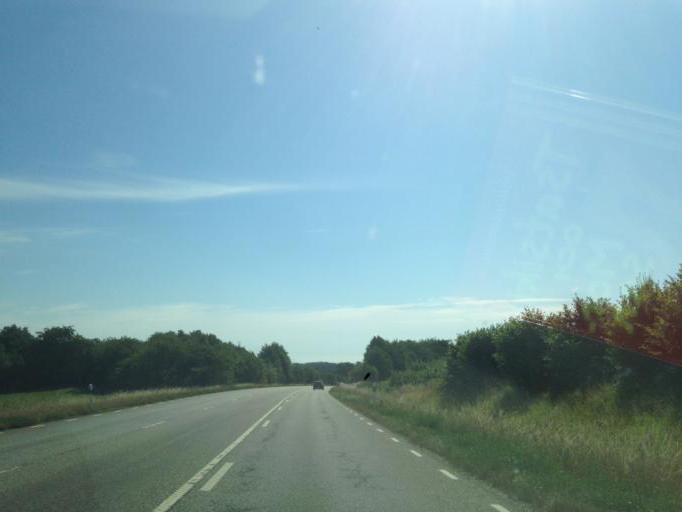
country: SE
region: Skane
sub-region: Simrishamns Kommun
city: Kivik
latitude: 55.6366
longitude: 14.2371
